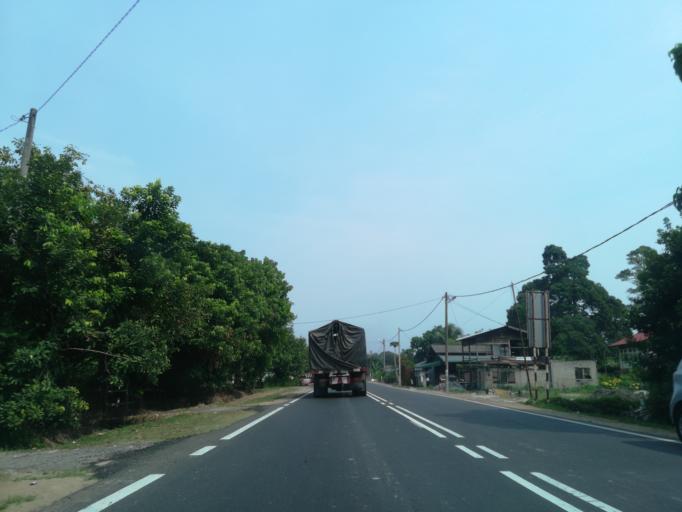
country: MY
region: Penang
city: Tasek Glugor
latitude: 5.4483
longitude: 100.5513
